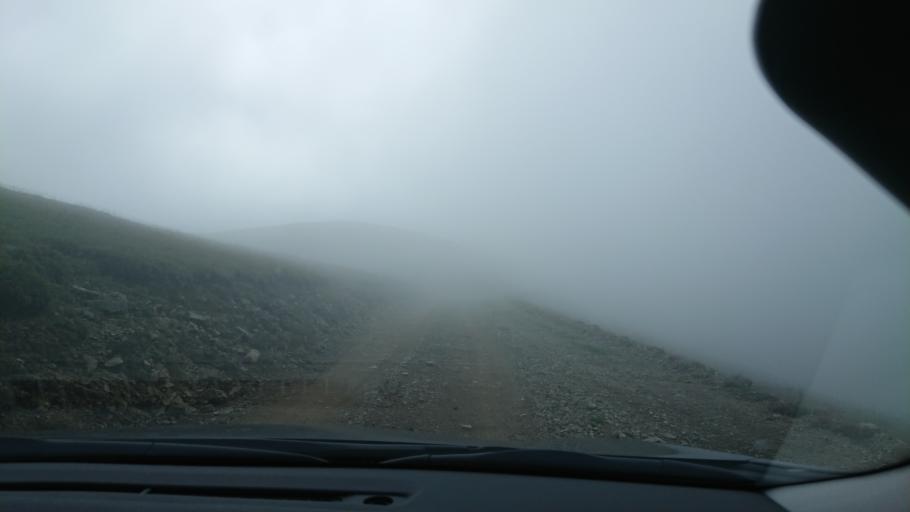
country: TR
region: Gumushane
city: Kurtun
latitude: 40.6234
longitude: 38.9928
